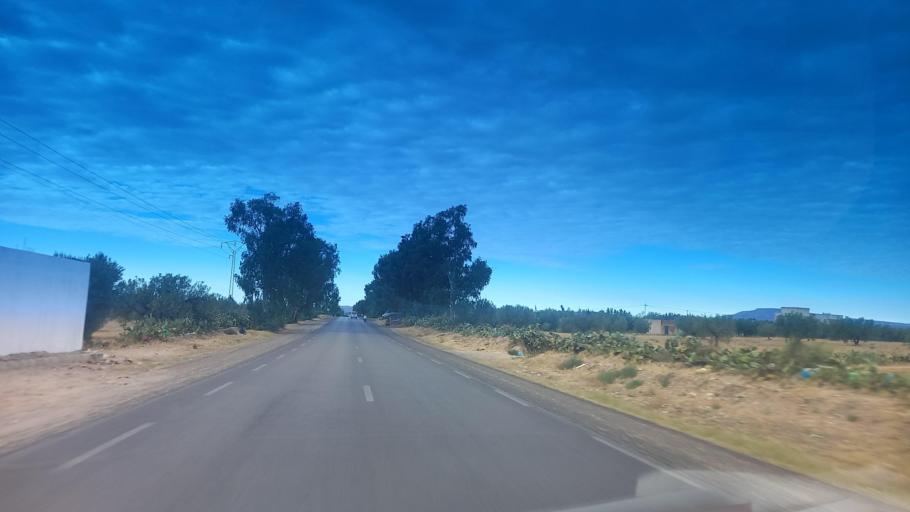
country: TN
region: Al Qasrayn
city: Sbiba
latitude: 35.2730
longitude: 9.0934
